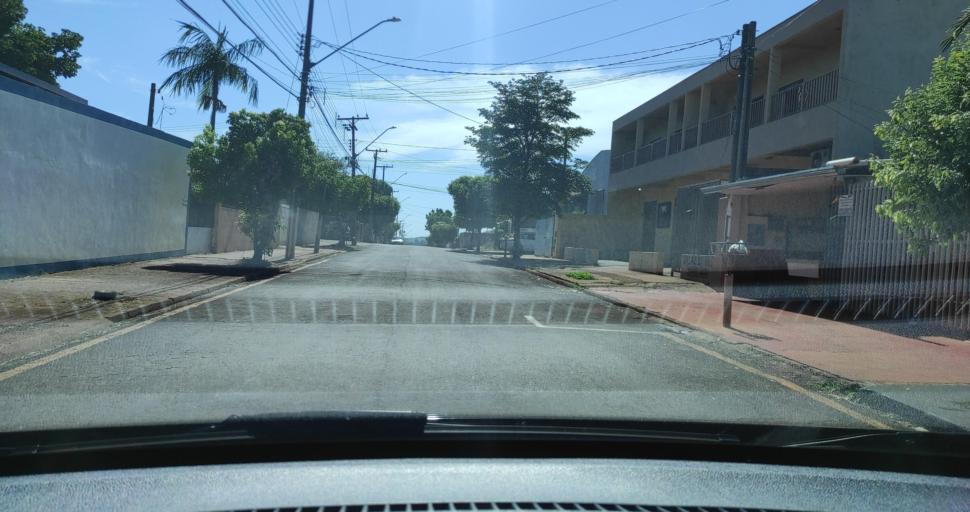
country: BR
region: Parana
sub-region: Ibipora
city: Ibipora
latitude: -23.2598
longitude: -51.0582
